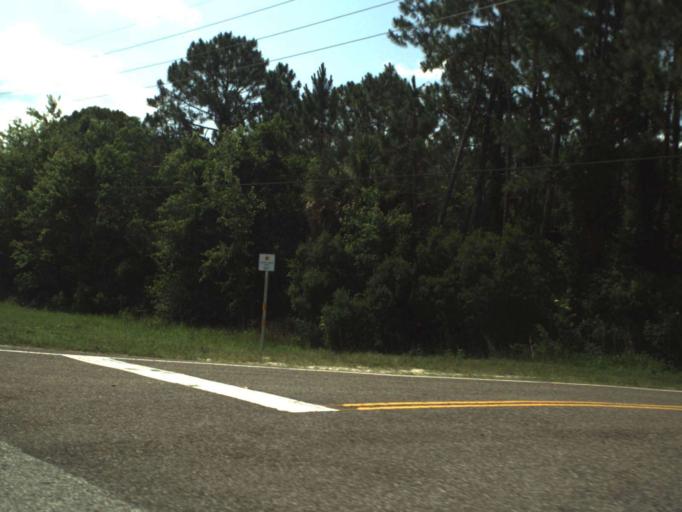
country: US
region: Florida
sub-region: Volusia County
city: Samsula-Spruce Creek
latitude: 29.0133
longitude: -81.0883
